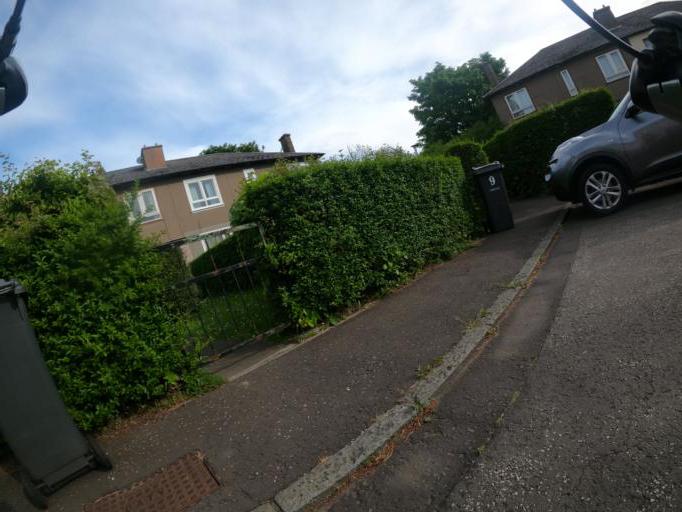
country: GB
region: Scotland
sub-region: Edinburgh
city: Edinburgh
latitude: 55.9736
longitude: -3.2173
